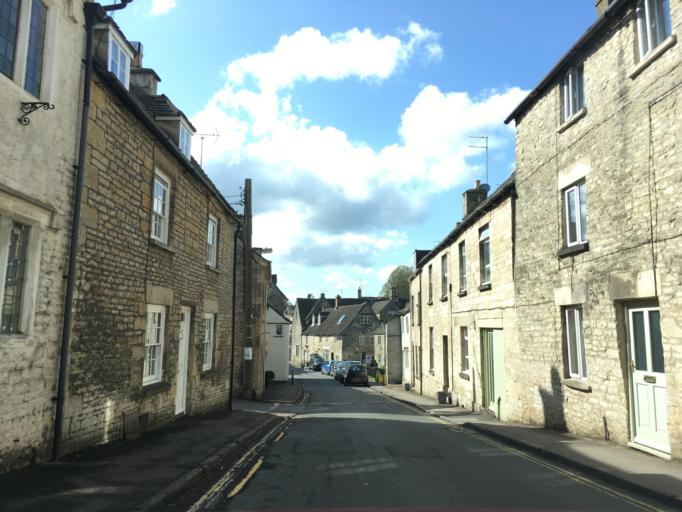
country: GB
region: England
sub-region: Gloucestershire
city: Minchinhampton
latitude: 51.7041
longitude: -2.1856
